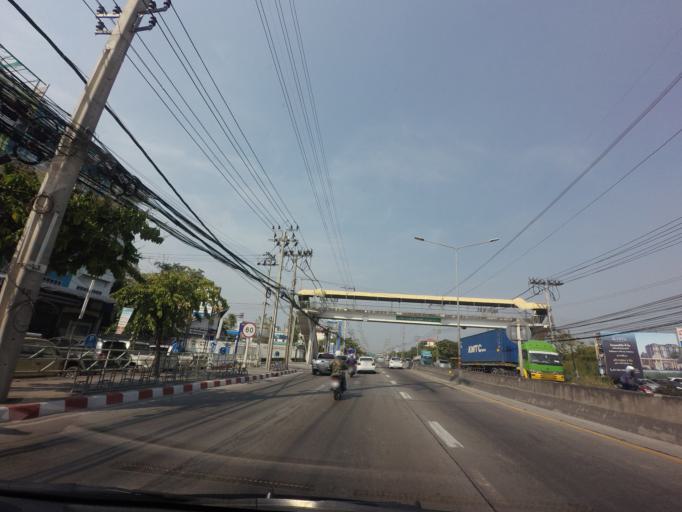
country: TH
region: Bangkok
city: Lat Krabang
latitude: 13.7485
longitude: 100.7465
